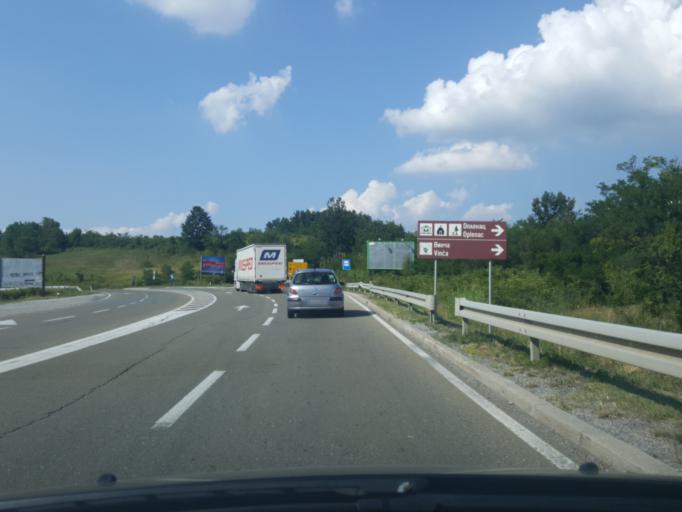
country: RS
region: Central Serbia
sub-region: Moravicki Okrug
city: Gornji Milanovac
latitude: 44.1202
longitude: 20.4831
